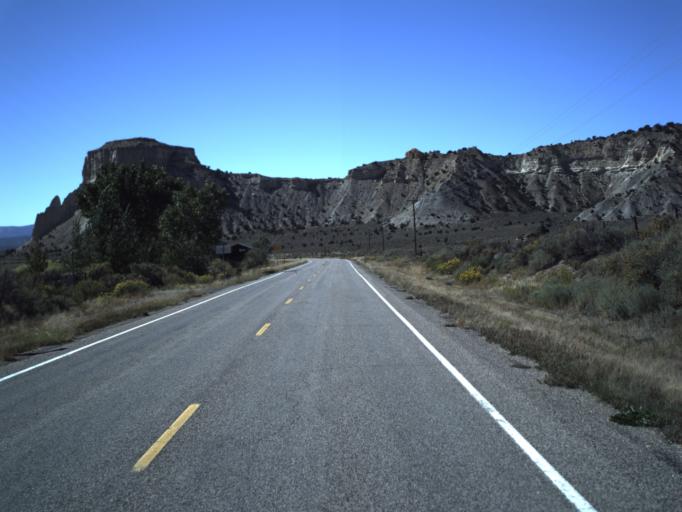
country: US
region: Utah
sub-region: Garfield County
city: Panguitch
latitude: 37.5627
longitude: -112.0067
